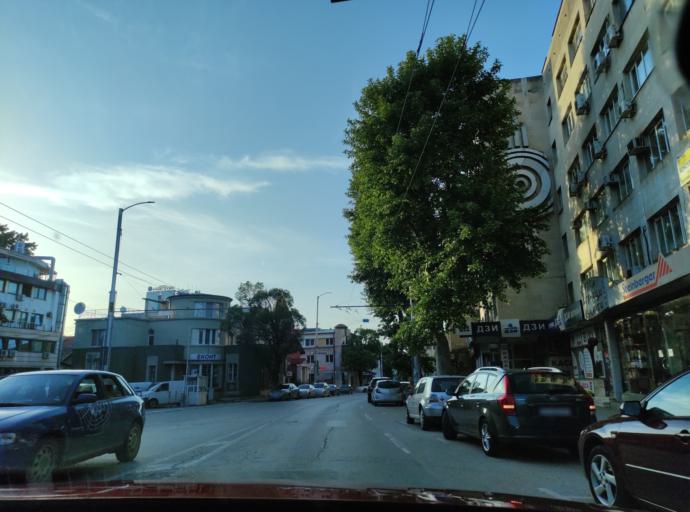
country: BG
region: Pleven
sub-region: Obshtina Pleven
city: Pleven
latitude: 43.4089
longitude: 24.6202
